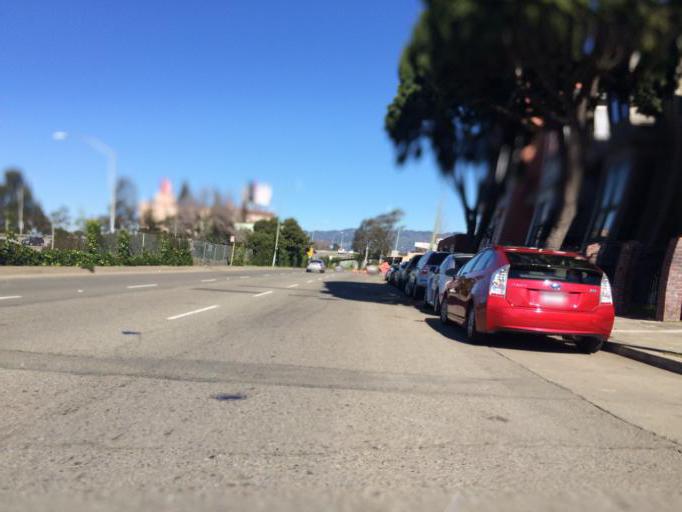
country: US
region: California
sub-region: Alameda County
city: Oakland
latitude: 37.8101
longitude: -122.2750
